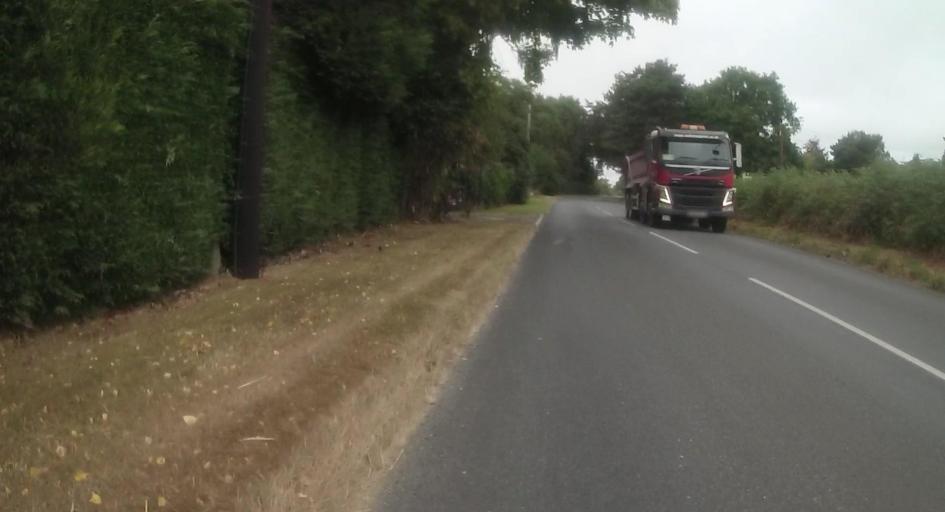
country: GB
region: England
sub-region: Dorset
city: Wareham
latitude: 50.6848
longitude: -2.1478
